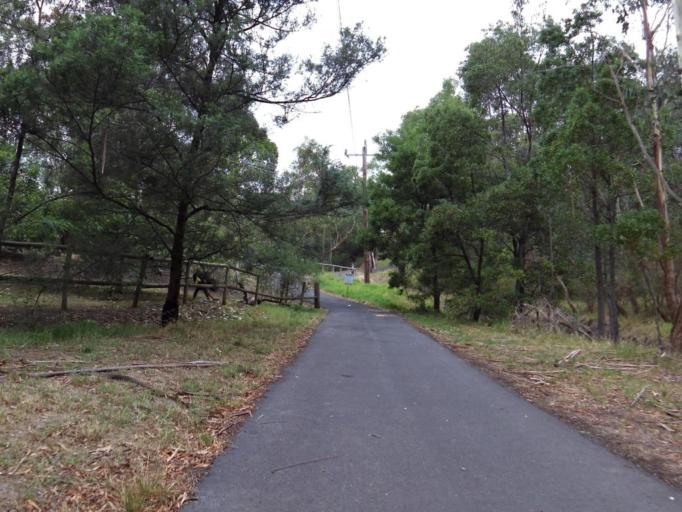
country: AU
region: Victoria
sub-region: Manningham
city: Templestowe Lower
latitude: -37.7634
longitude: 145.1271
